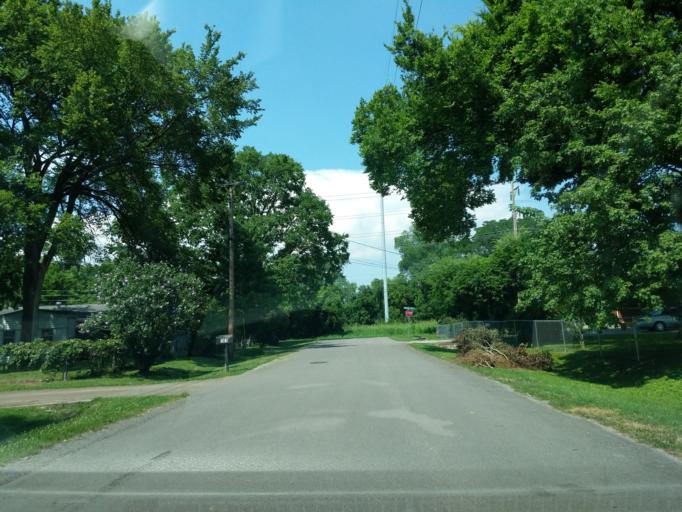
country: US
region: Tennessee
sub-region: Davidson County
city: Lakewood
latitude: 36.2800
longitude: -86.6741
